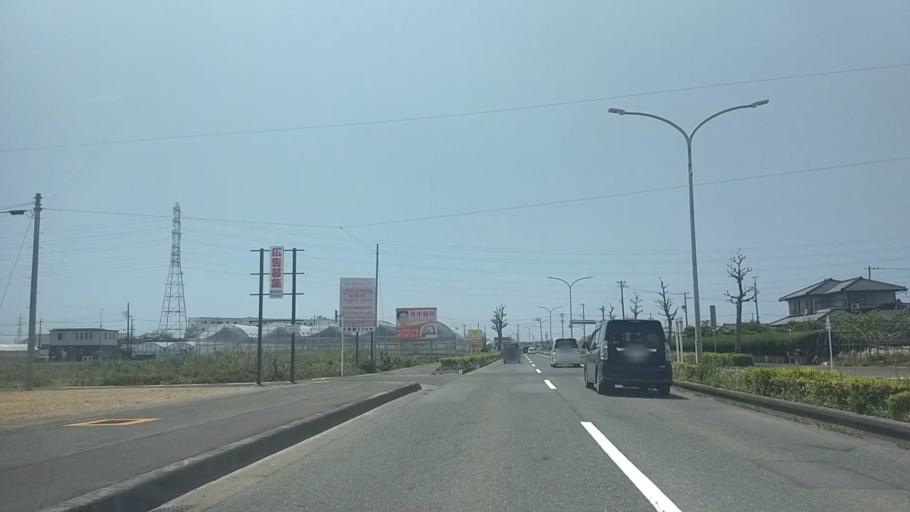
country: JP
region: Shizuoka
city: Hamamatsu
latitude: 34.7362
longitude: 137.6630
